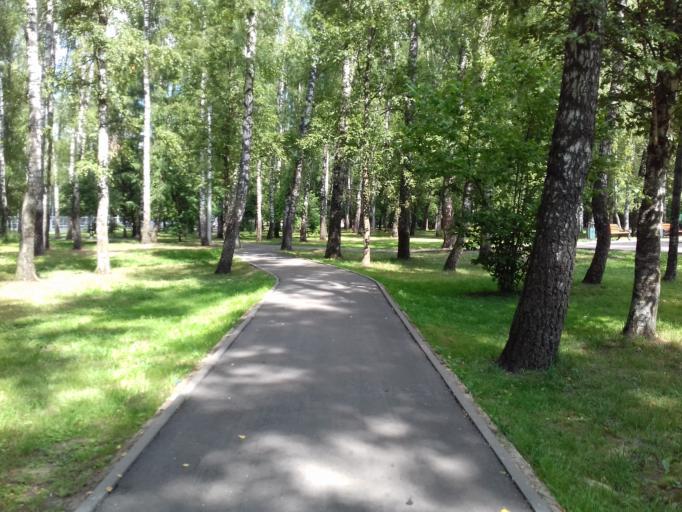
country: RU
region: Tula
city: Tula
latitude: 54.1809
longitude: 37.5863
